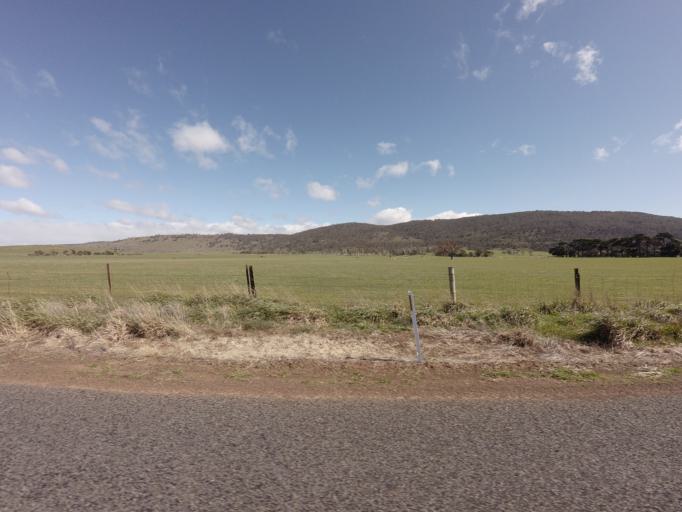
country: AU
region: Tasmania
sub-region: Northern Midlands
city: Evandale
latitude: -41.9853
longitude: 147.4506
